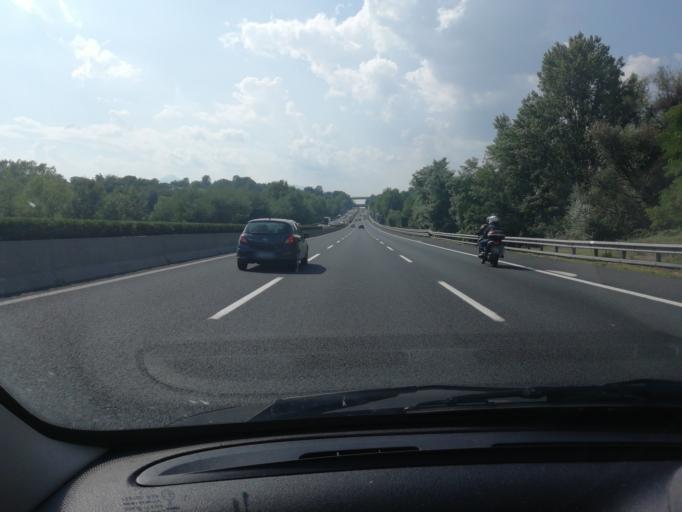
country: IT
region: Latium
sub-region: Provincia di Frosinone
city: Arnara
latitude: 41.5662
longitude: 13.3932
